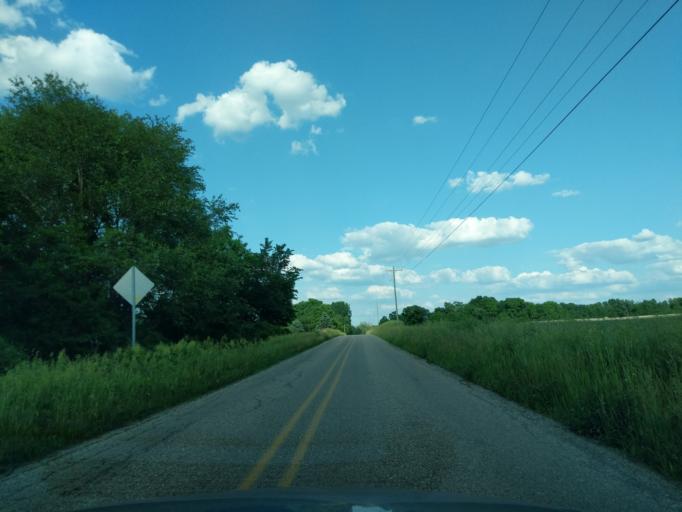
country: US
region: Indiana
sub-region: Kosciusko County
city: North Webster
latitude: 41.3025
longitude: -85.5976
